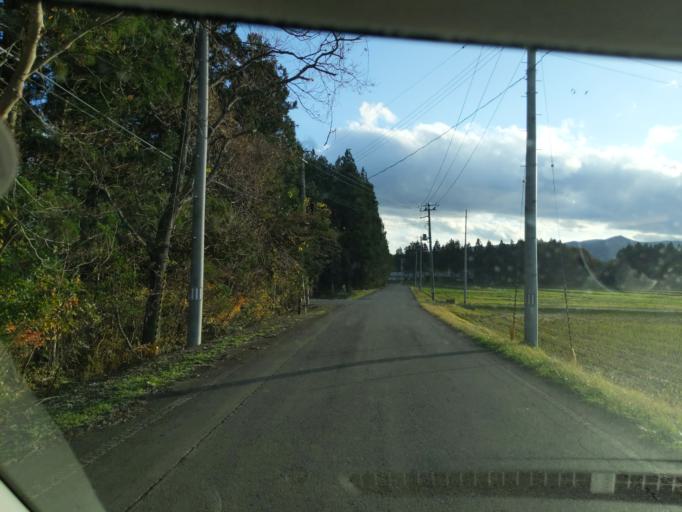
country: JP
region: Iwate
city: Mizusawa
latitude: 39.1049
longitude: 140.9983
